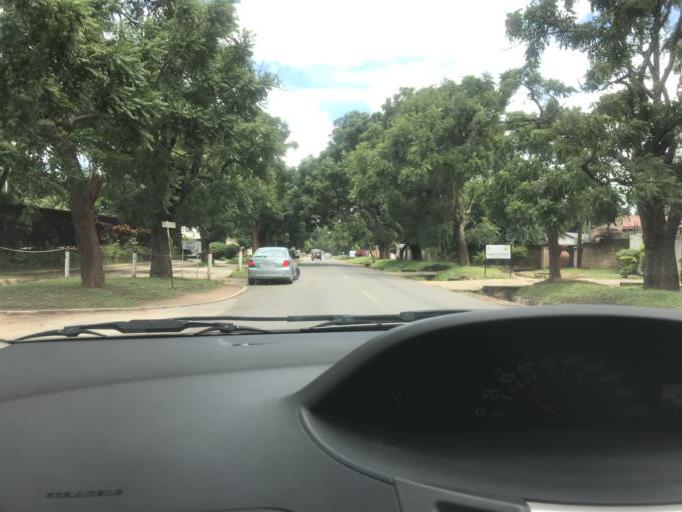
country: ZM
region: Lusaka
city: Lusaka
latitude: -15.4227
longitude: 28.3121
